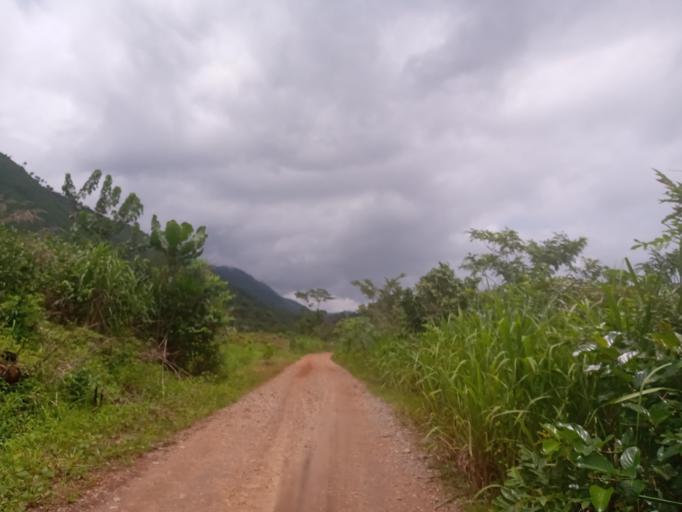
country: SL
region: Northern Province
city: Bumbuna
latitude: 8.9709
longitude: -11.7545
